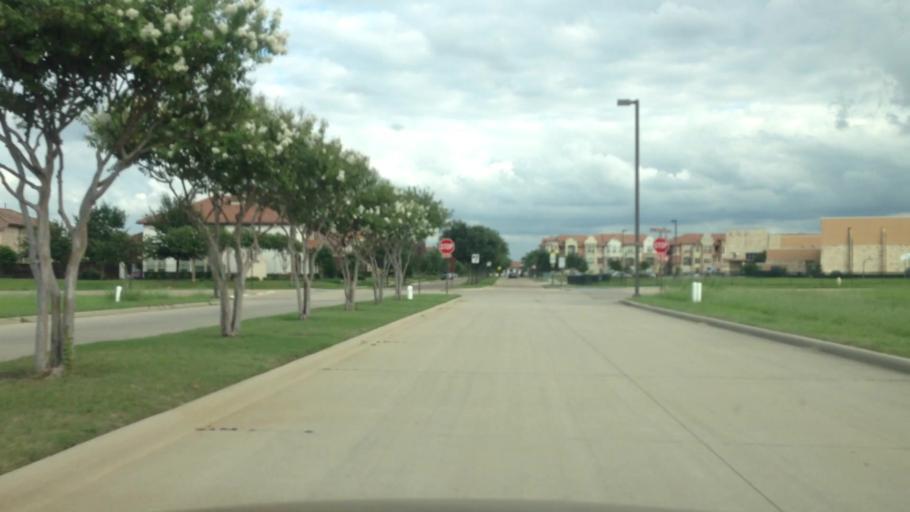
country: US
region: Texas
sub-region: Dallas County
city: Farmers Branch
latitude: 32.9050
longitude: -96.9382
